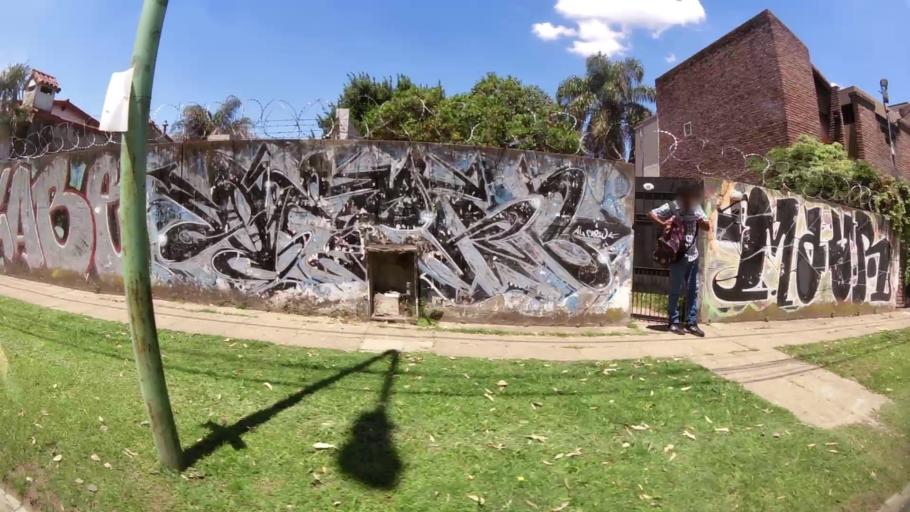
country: AR
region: Buenos Aires
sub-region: Partido de Merlo
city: Merlo
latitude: -34.6620
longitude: -58.6997
